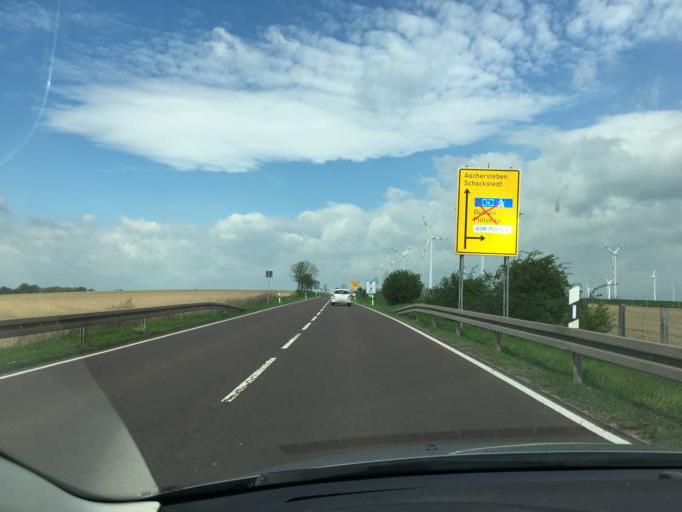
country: DE
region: Saxony-Anhalt
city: Alsleben
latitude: 51.7096
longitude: 11.6584
